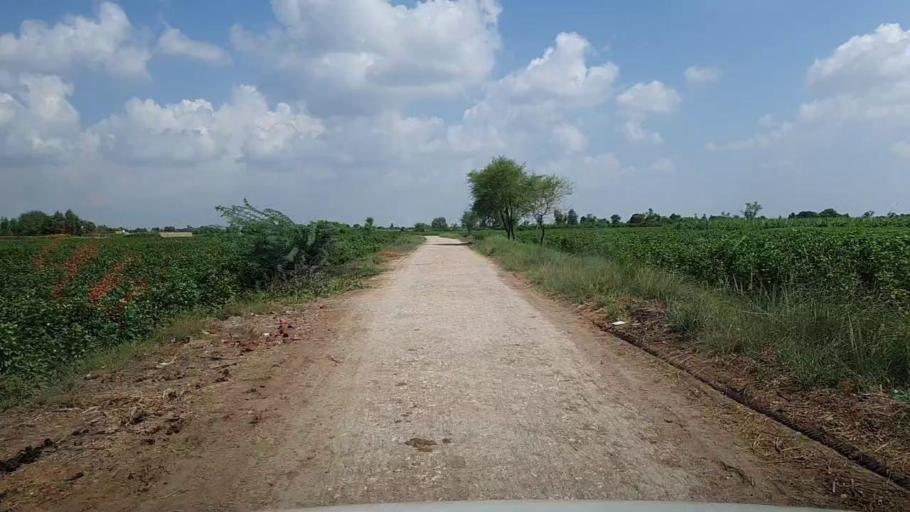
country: PK
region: Sindh
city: Kandiaro
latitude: 27.0026
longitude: 68.3066
